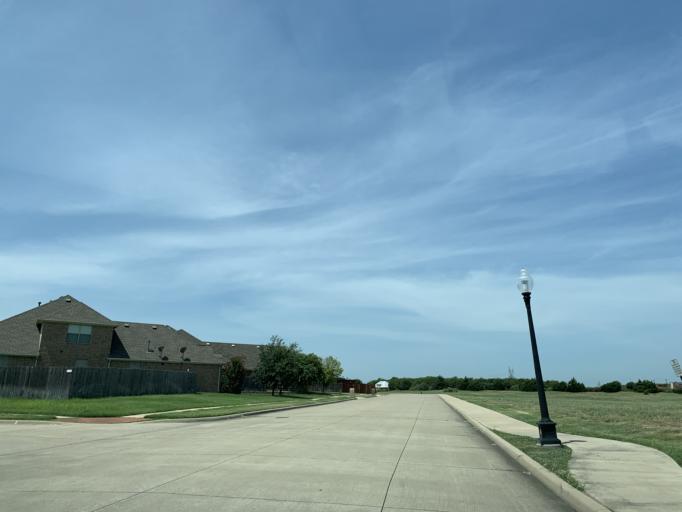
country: US
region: Texas
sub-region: Dallas County
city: Cedar Hill
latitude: 32.6462
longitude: -97.0404
